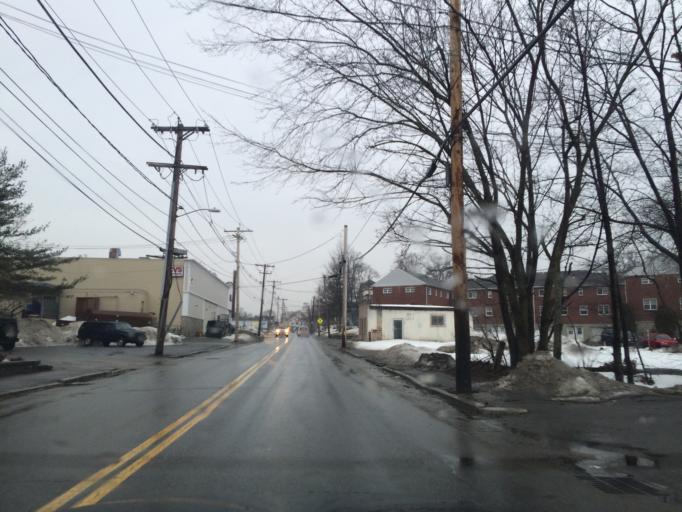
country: US
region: Massachusetts
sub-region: Middlesex County
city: Waltham
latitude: 42.3795
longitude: -71.2222
